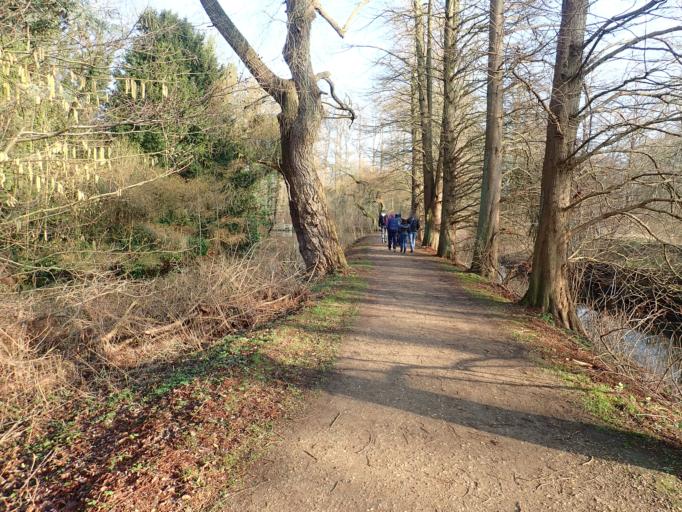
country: BE
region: Flanders
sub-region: Provincie Antwerpen
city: Borsbeek
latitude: 51.2143
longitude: 4.4705
